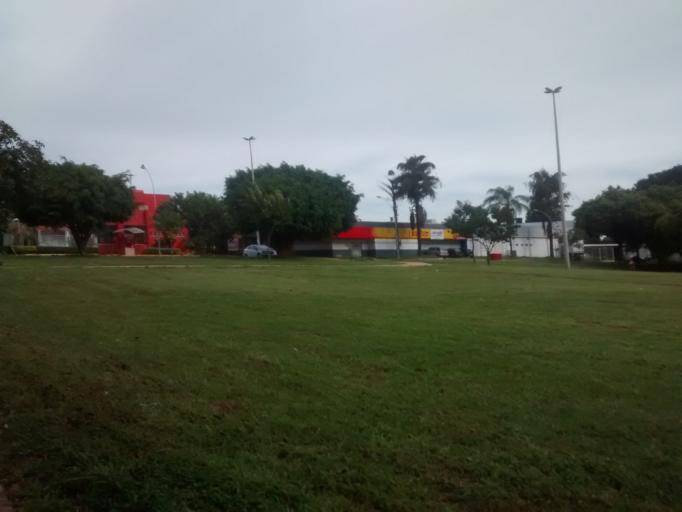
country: BR
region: Federal District
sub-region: Brasilia
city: Brasilia
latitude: -15.7722
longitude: -47.8874
